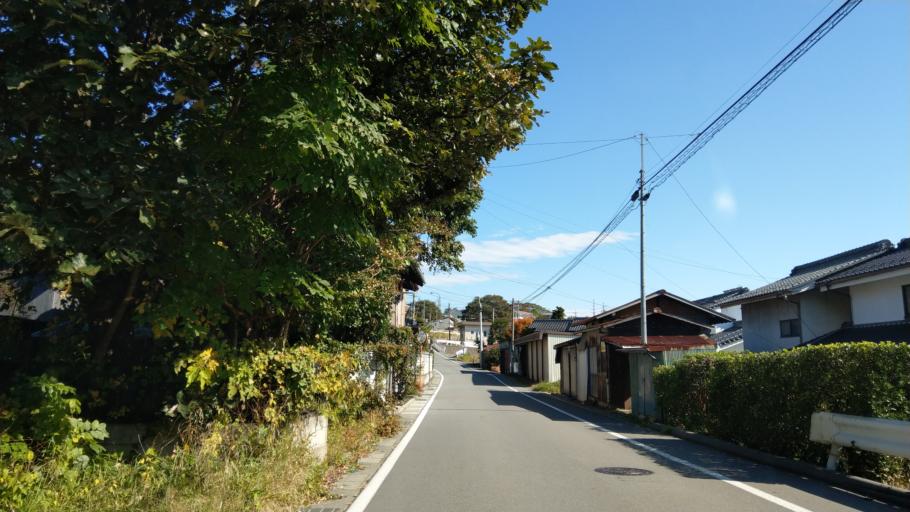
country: JP
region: Nagano
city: Komoro
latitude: 36.3213
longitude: 138.4355
